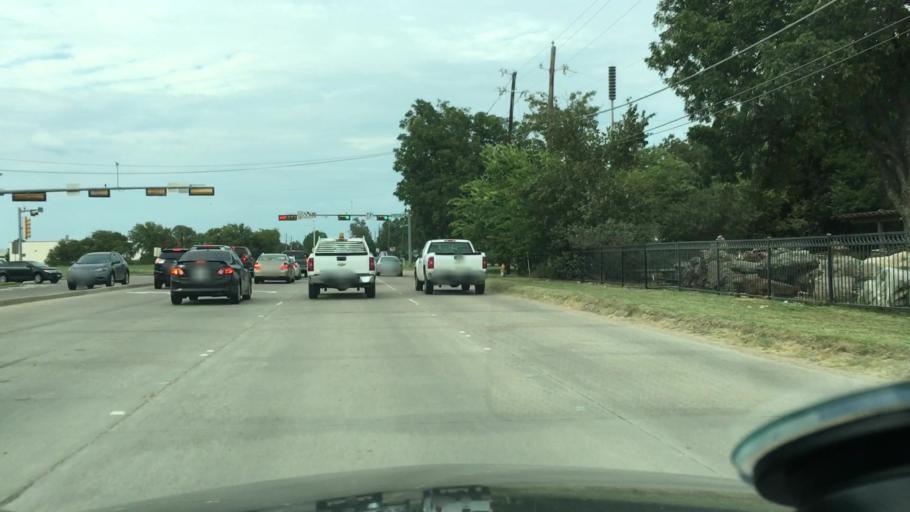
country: US
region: Texas
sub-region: Collin County
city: Allen
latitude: 33.0647
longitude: -96.6885
